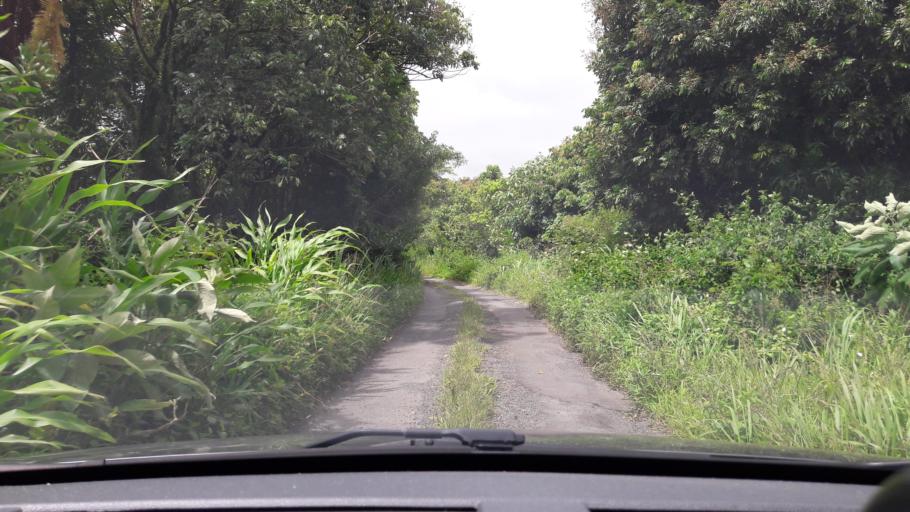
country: RE
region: Reunion
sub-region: Reunion
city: Saint-Benoit
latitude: -21.0983
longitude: 55.6972
